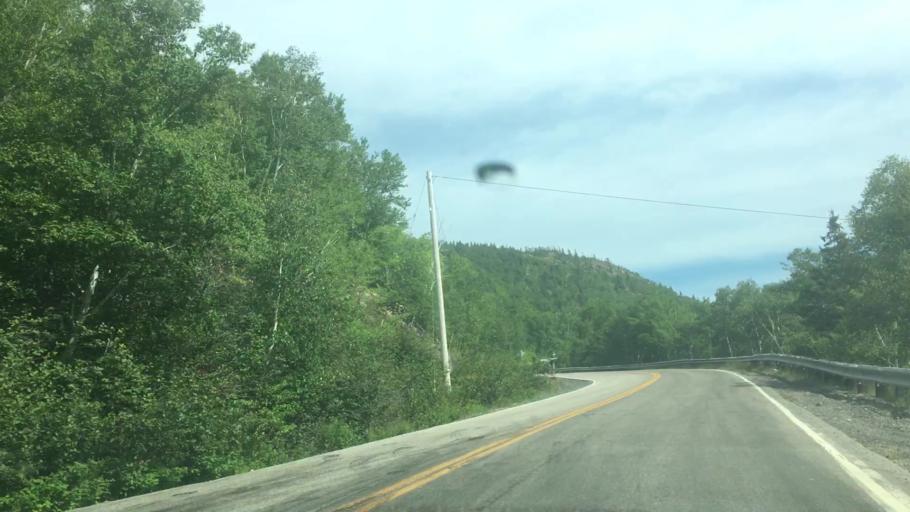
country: CA
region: Nova Scotia
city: Sydney Mines
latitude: 46.5835
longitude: -60.3962
